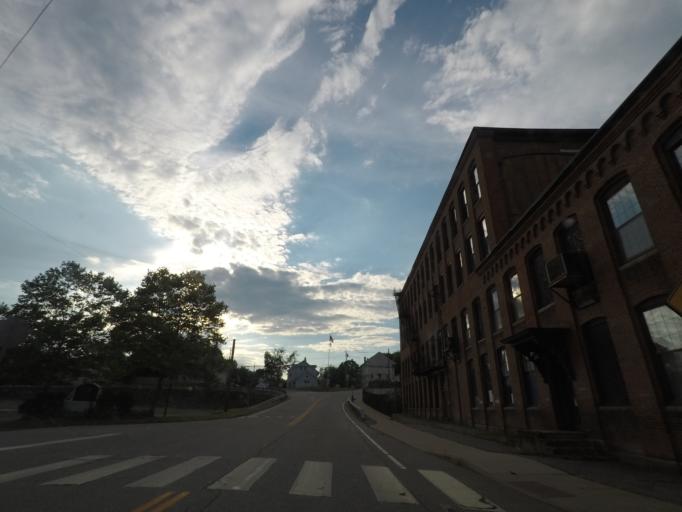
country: US
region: Connecticut
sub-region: Windham County
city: North Grosvenor Dale
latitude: 41.9857
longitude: -71.8981
